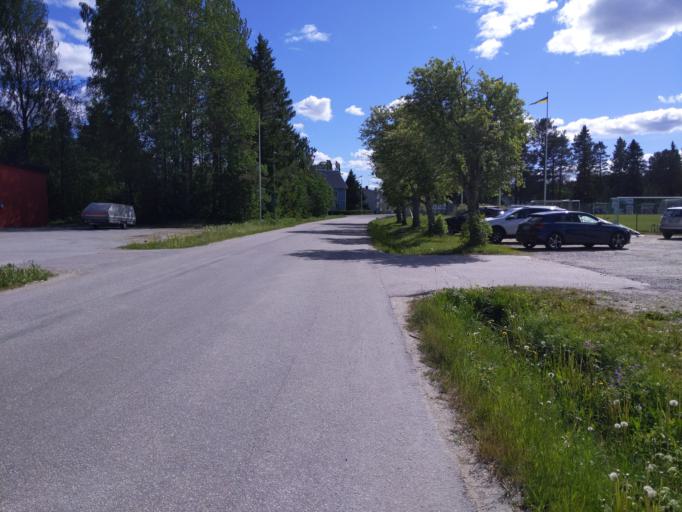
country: SE
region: Vaesternorrland
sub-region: OErnskoeldsviks Kommun
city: Kopmanholmen
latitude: 63.1714
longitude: 18.5666
